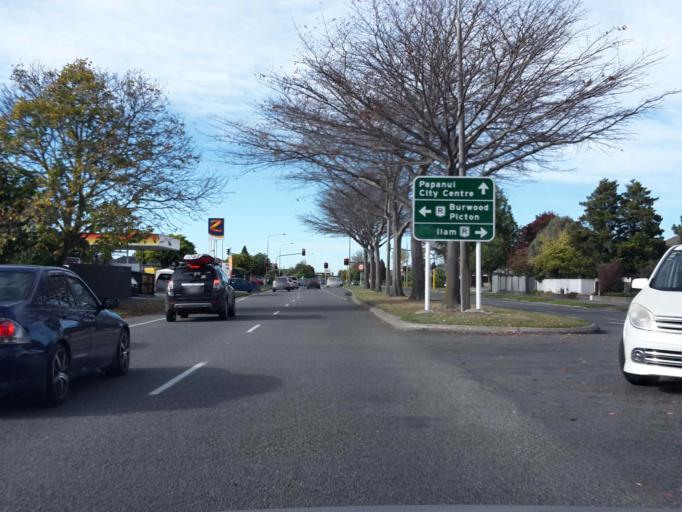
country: NZ
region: Canterbury
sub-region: Christchurch City
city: Christchurch
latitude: -43.4896
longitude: 172.5920
